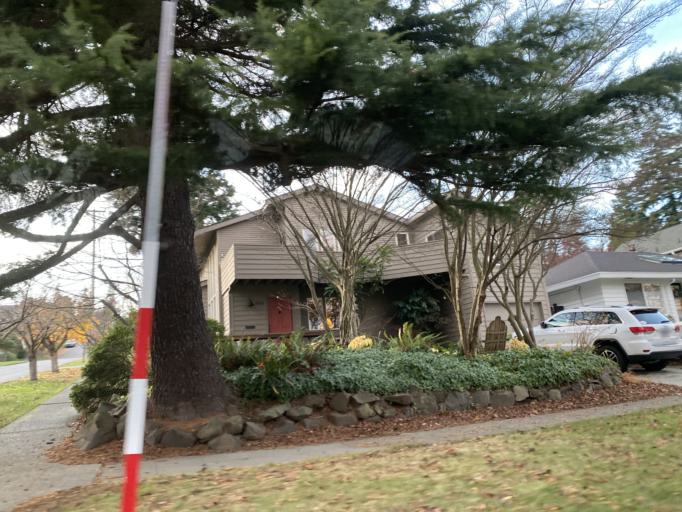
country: US
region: Washington
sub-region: King County
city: Seattle
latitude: 47.6469
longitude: -122.4023
